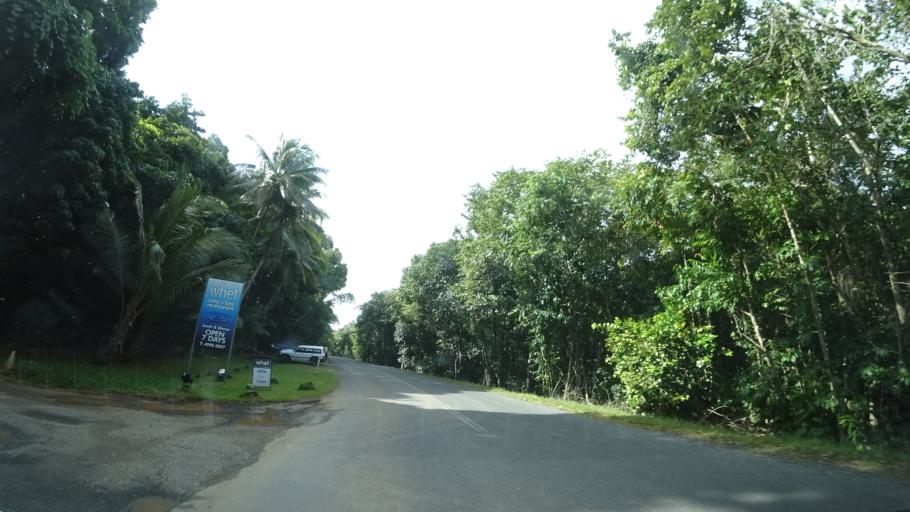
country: AU
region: Queensland
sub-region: Cairns
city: Port Douglas
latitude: -16.0909
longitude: 145.4614
